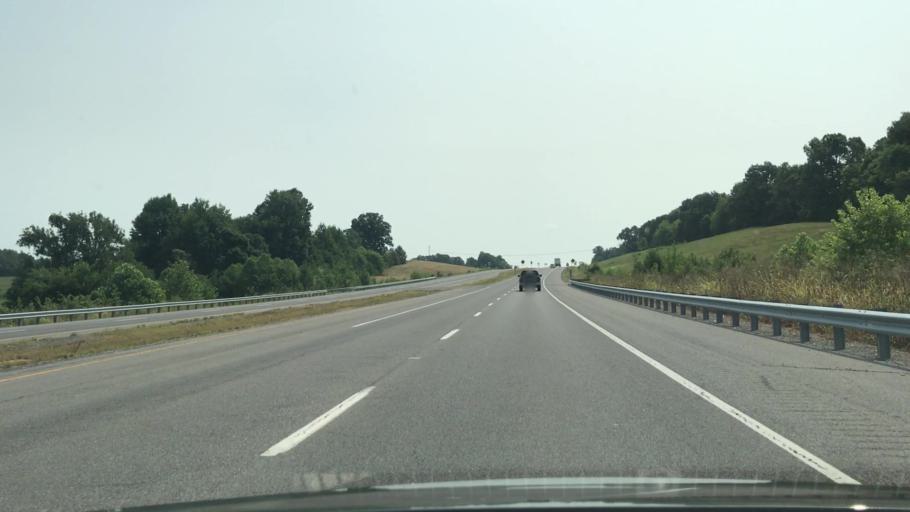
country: US
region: Kentucky
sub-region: Calloway County
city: Murray
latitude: 36.6514
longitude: -88.2777
